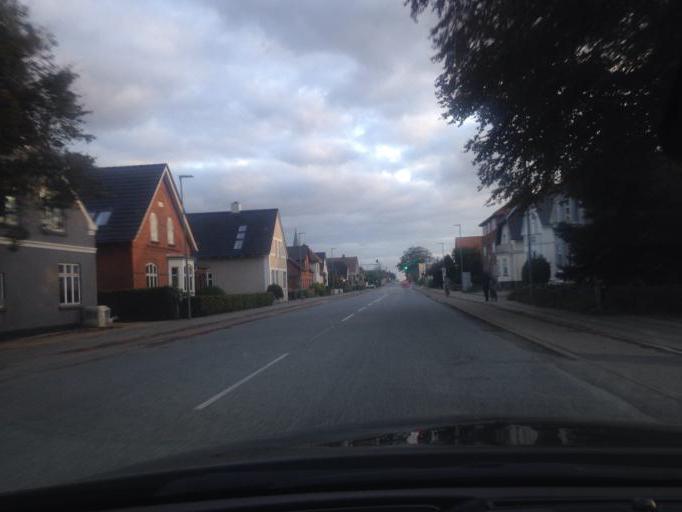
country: DK
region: South Denmark
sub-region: Kolding Kommune
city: Kolding
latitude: 55.4798
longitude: 9.4687
